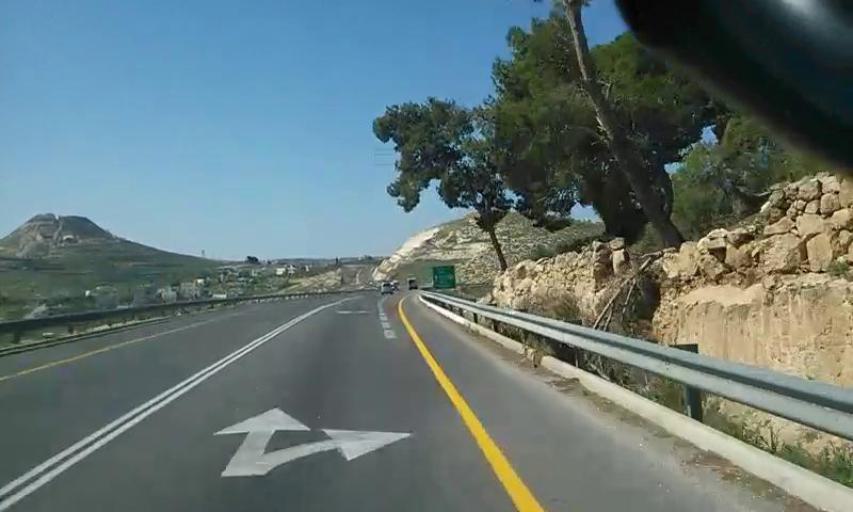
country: PS
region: West Bank
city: Bayt Ta`mar
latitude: 31.6702
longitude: 35.2391
